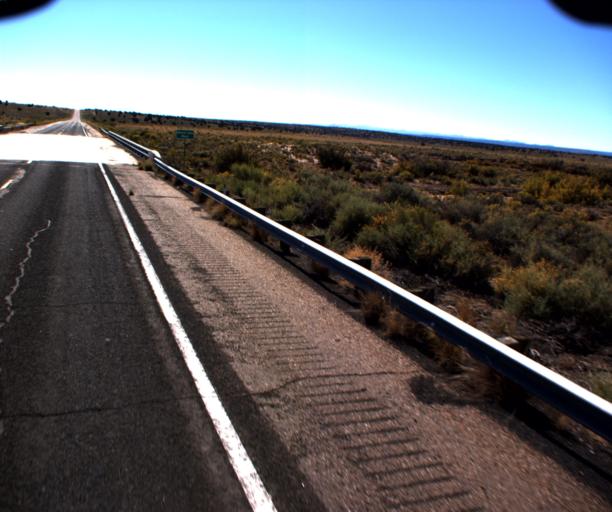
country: US
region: Arizona
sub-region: Navajo County
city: Snowflake
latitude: 34.6697
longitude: -109.7238
